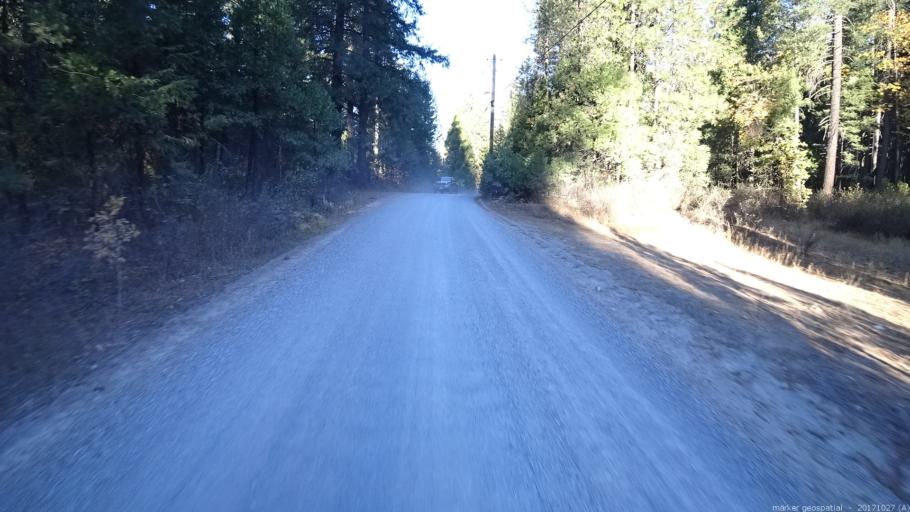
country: US
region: California
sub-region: Shasta County
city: Burney
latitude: 40.9943
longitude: -121.8836
